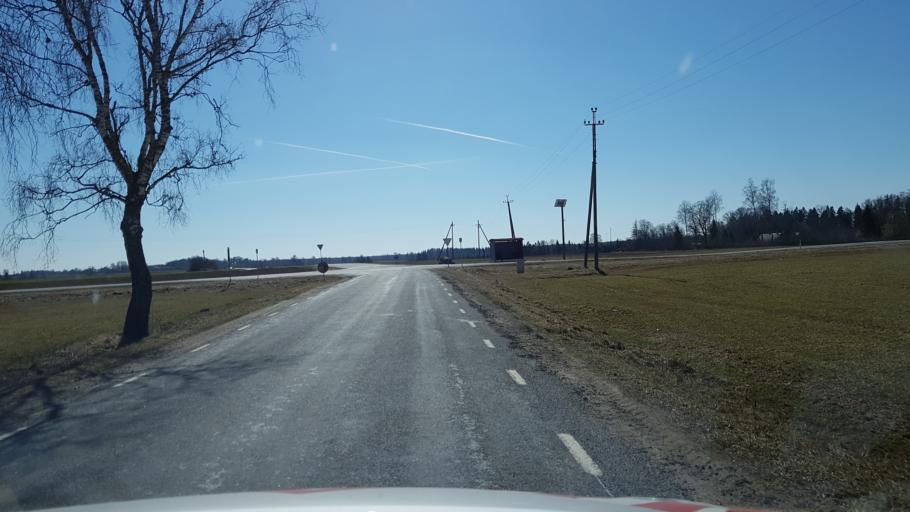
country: EE
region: Laeaene-Virumaa
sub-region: Vaeike-Maarja vald
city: Vaike-Maarja
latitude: 59.0942
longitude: 26.1949
